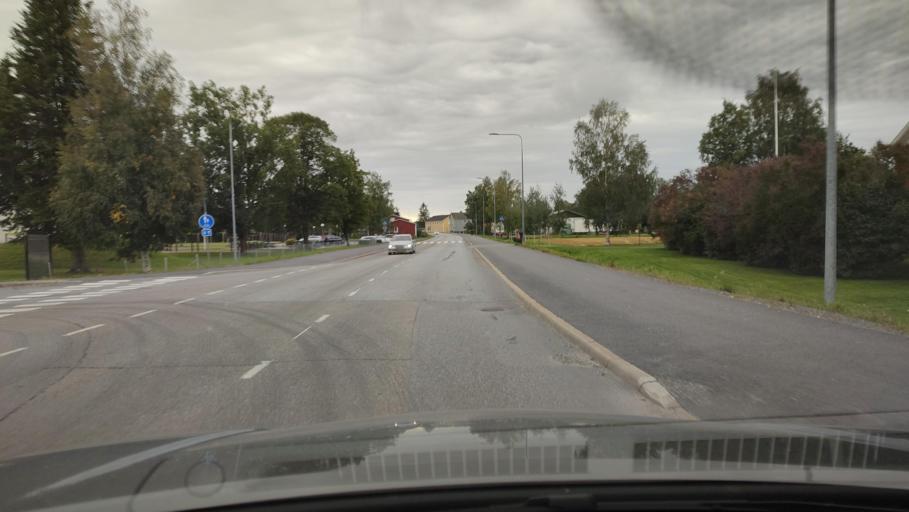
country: FI
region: Ostrobothnia
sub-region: Sydosterbotten
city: Kristinestad
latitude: 62.2548
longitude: 21.5255
